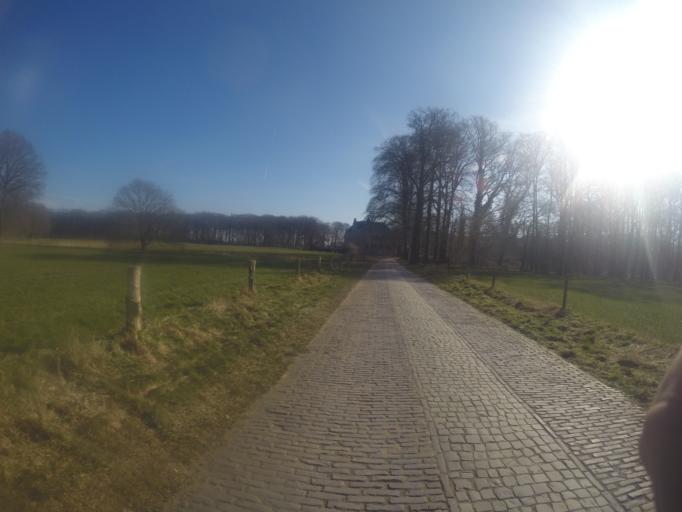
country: NL
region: Gelderland
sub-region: Gemeente Bronckhorst
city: Hengelo
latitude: 52.1022
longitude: 6.3200
